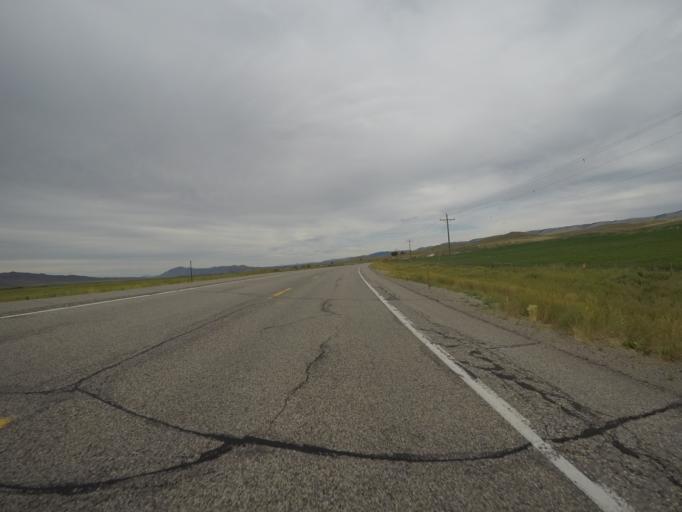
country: US
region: Utah
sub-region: Rich County
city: Randolph
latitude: 41.9911
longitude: -110.9416
